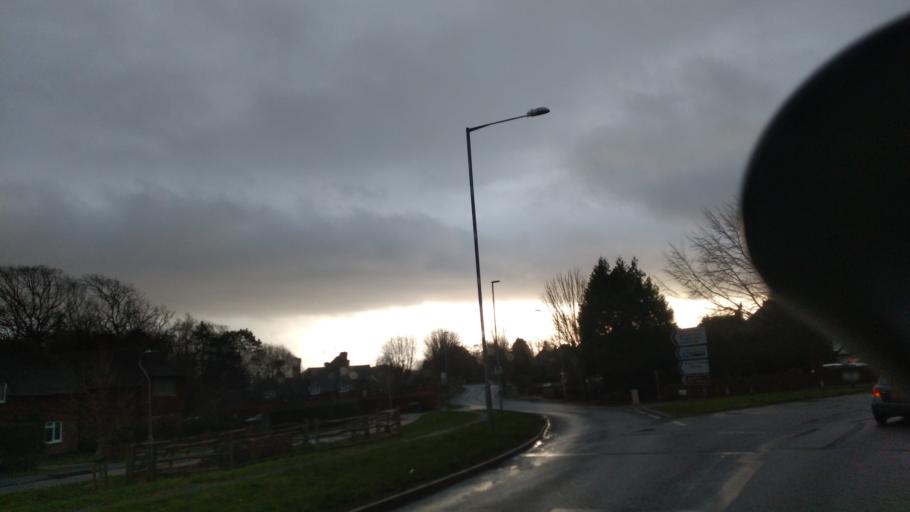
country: GB
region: England
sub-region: East Sussex
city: Eastbourne
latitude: 50.7953
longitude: 0.2575
